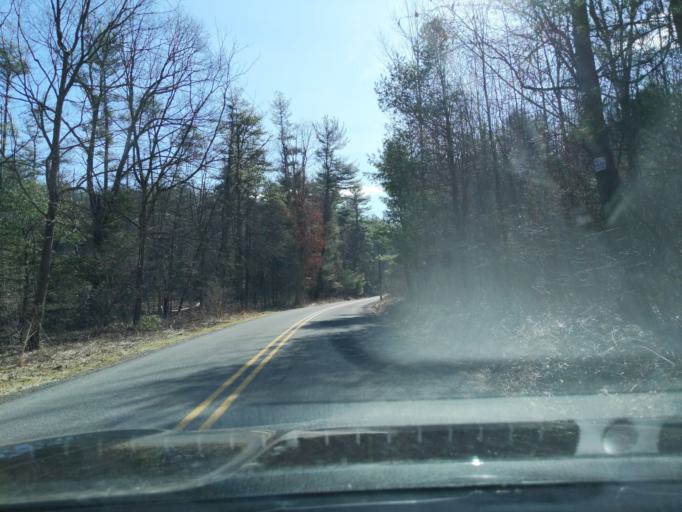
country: US
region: Pennsylvania
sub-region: Blair County
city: Williamsburg
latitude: 40.3780
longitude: -78.2475
